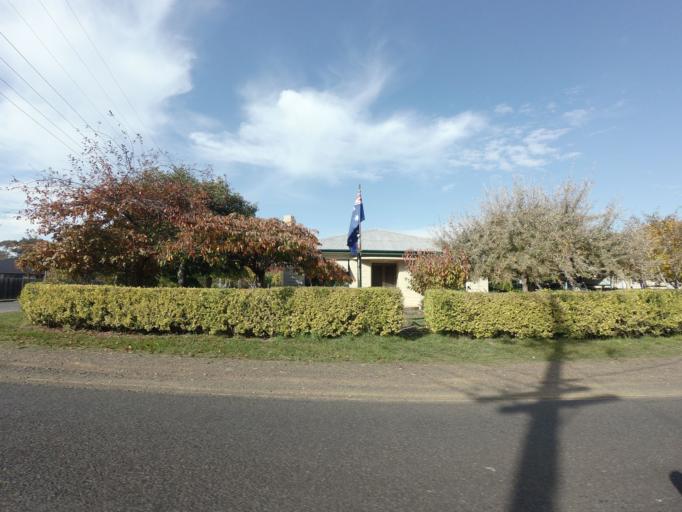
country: AU
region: Tasmania
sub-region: Northern Midlands
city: Longford
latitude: -41.5324
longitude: 146.9995
